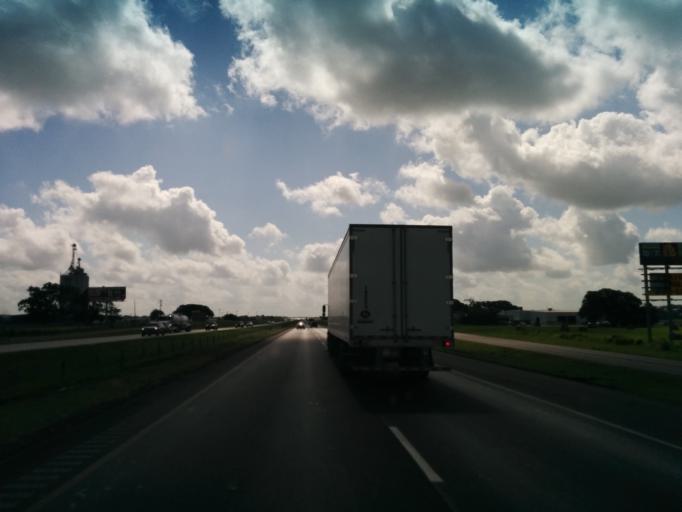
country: US
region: Texas
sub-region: Colorado County
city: Weimar
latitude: 29.6921
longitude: -96.7660
